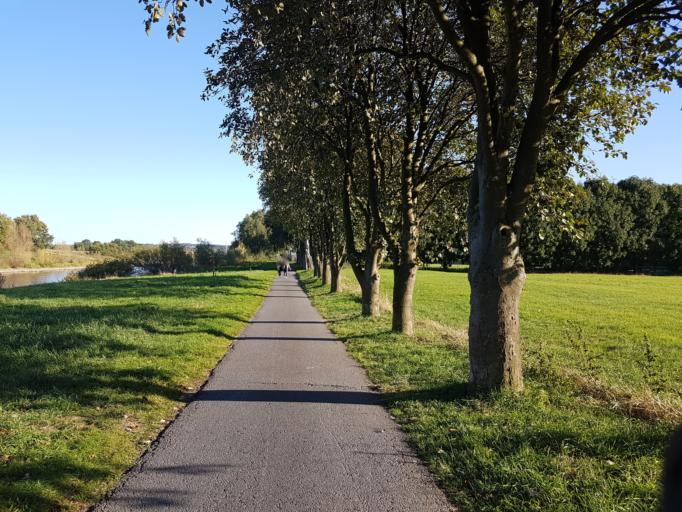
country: DE
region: North Rhine-Westphalia
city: Bad Oeynhausen
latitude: 52.2199
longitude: 8.8283
